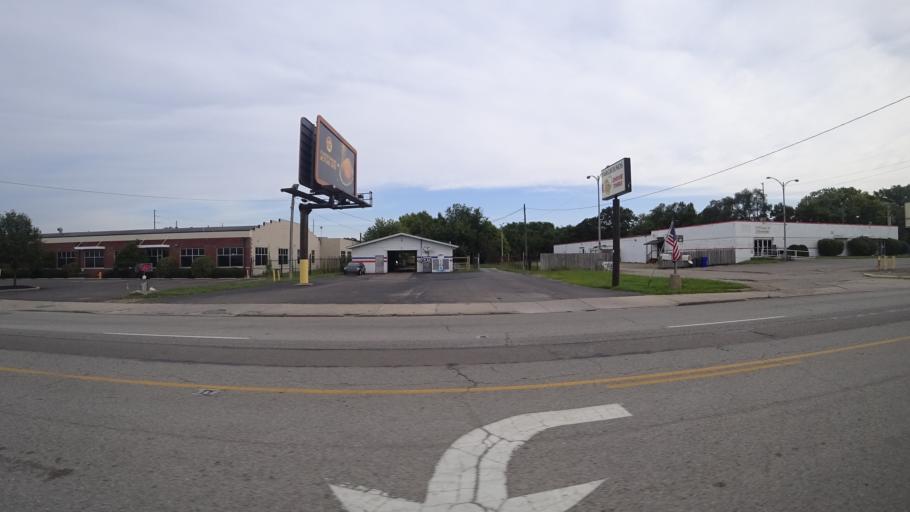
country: US
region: Ohio
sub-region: Butler County
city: Hamilton
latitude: 39.4029
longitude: -84.5353
